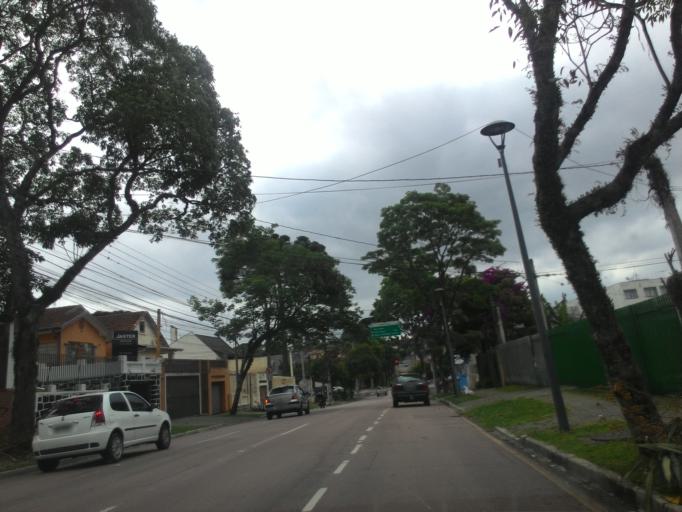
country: BR
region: Parana
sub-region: Curitiba
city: Curitiba
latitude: -25.4169
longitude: -49.2729
